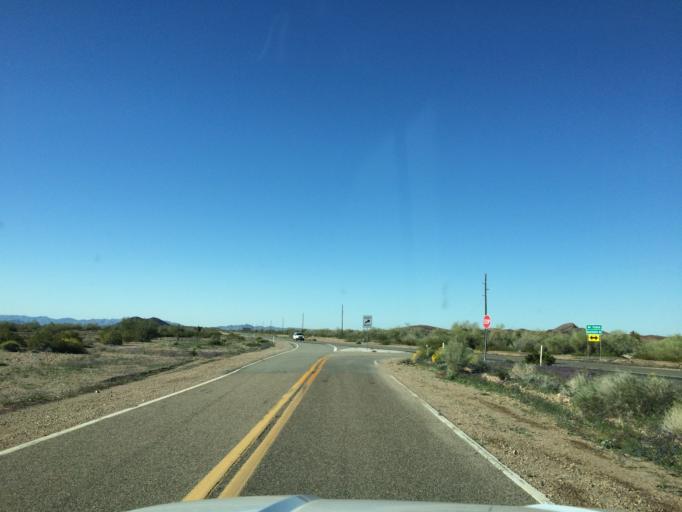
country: US
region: Arizona
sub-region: Yuma County
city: Wellton
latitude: 32.9619
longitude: -114.2928
